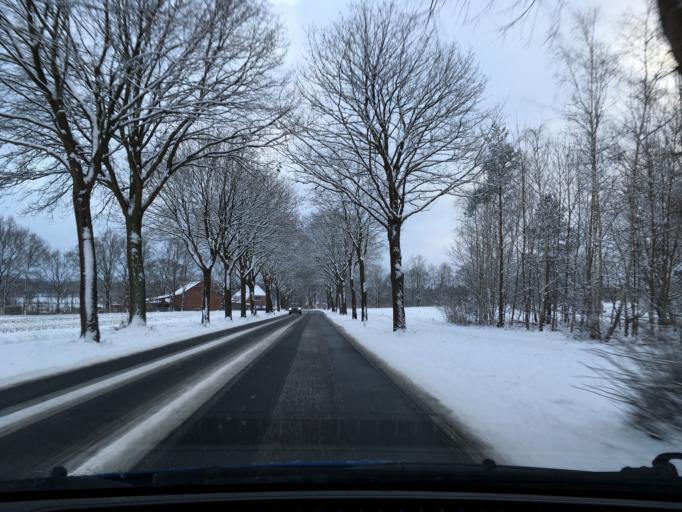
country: DE
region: Lower Saxony
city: Wulfsen
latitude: 53.3060
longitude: 10.1609
